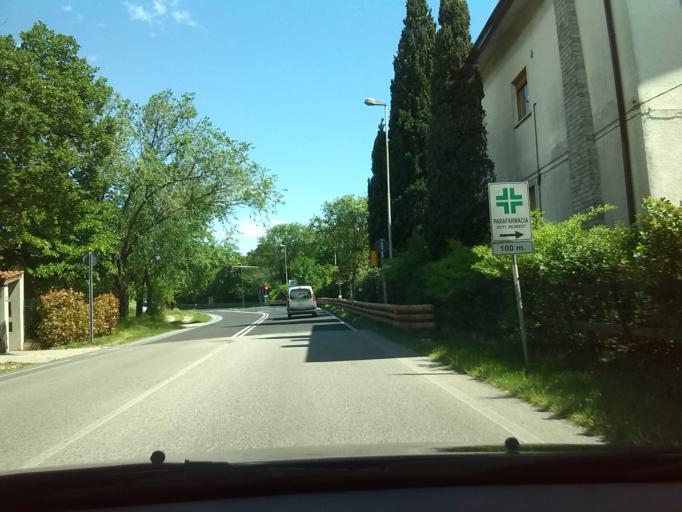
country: IT
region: Friuli Venezia Giulia
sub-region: Provincia di Trieste
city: Duino
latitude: 45.7748
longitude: 13.6078
